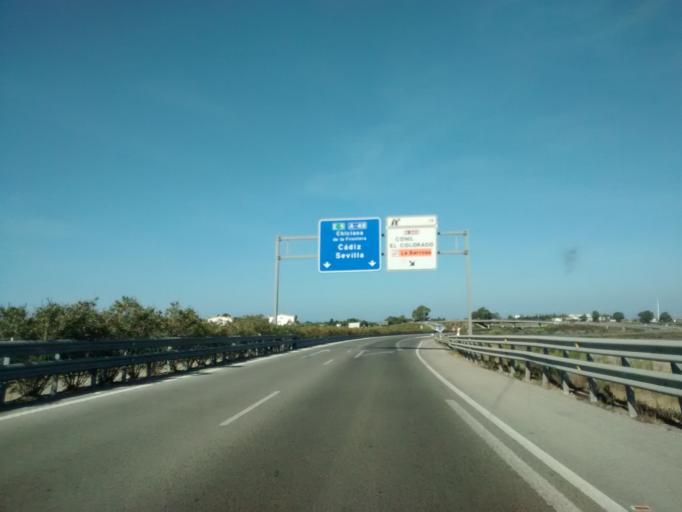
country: ES
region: Andalusia
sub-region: Provincia de Cadiz
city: Conil de la Frontera
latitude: 36.3556
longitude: -6.0975
